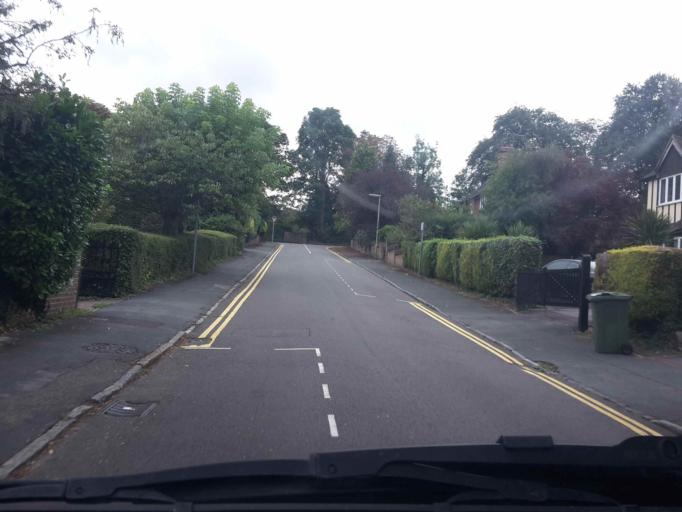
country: GB
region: England
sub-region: Surrey
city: Guildford
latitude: 51.2343
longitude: -0.5906
